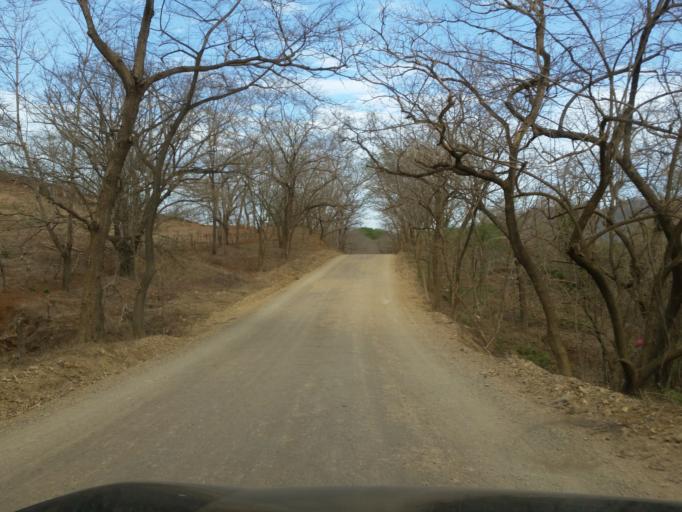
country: NI
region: Rivas
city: Tola
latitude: 11.4089
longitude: -86.0075
